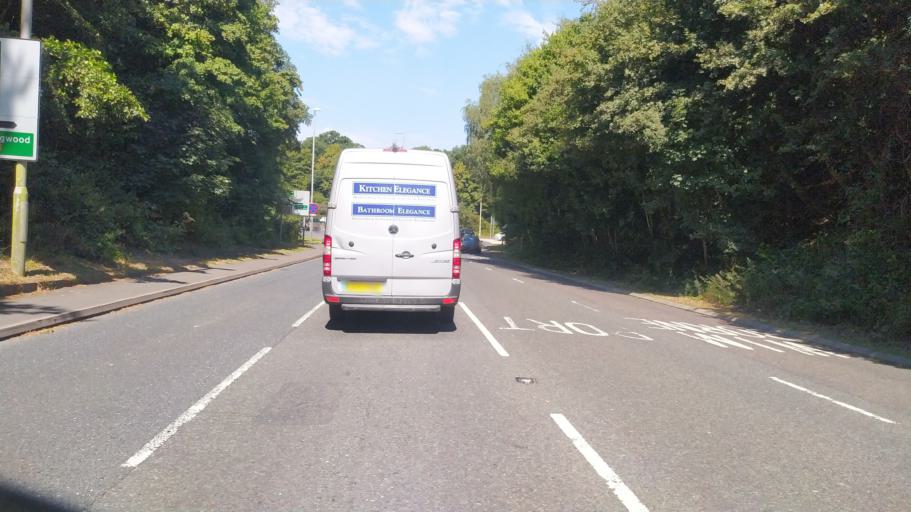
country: GB
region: England
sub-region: Dorset
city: Wimborne Minster
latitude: 50.7861
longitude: -1.9784
